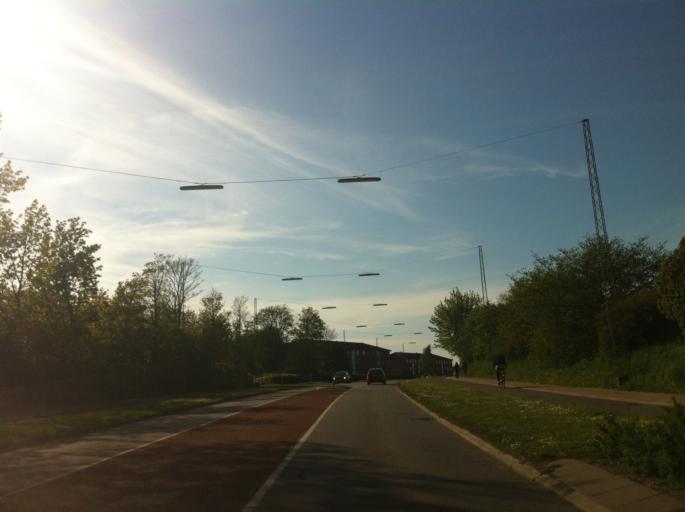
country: DK
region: Zealand
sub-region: Naestved Kommune
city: Naestved
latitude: 55.2045
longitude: 11.7709
